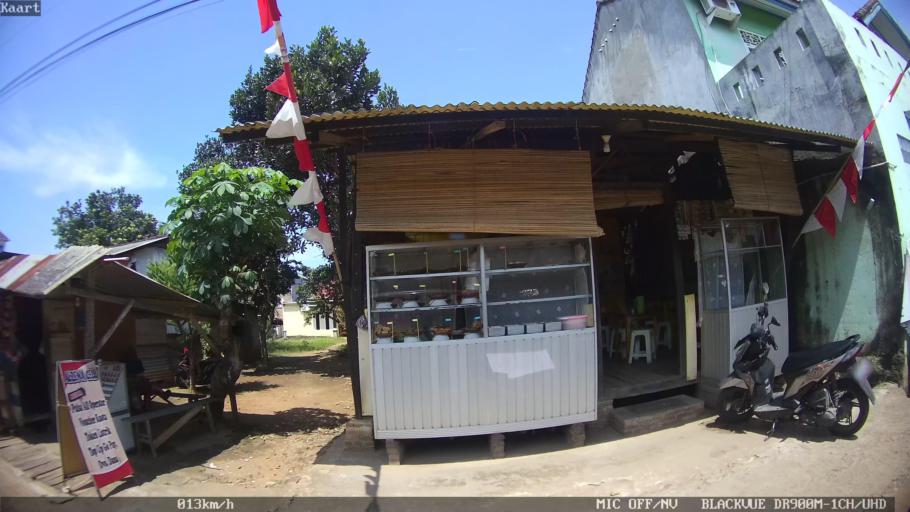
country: ID
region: Lampung
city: Kedaton
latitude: -5.3644
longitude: 105.2487
